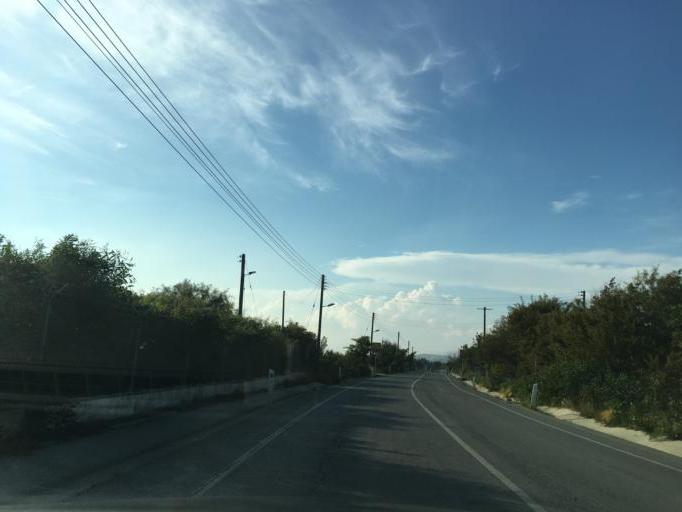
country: CY
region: Larnaka
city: Kofinou
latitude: 34.7338
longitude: 33.3344
